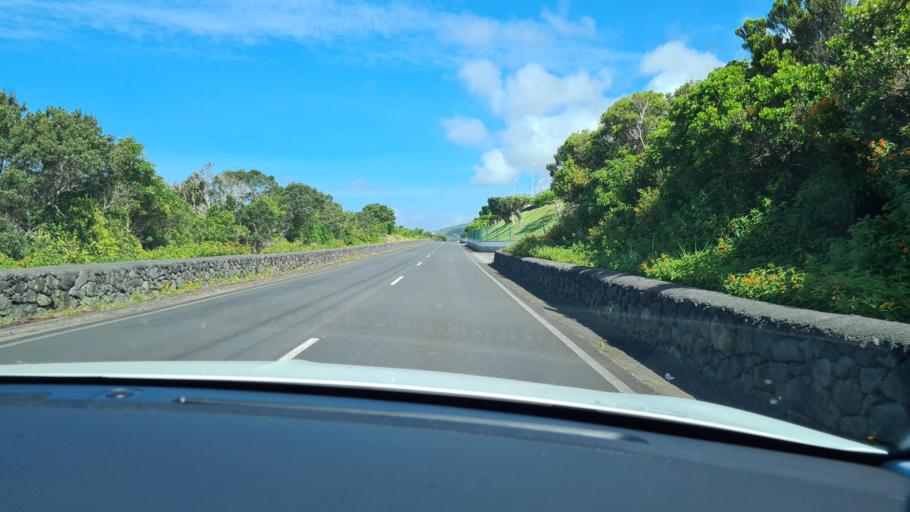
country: PT
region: Azores
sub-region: Sao Roque do Pico
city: Sao Roque do Pico
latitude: 38.6534
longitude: -28.1502
